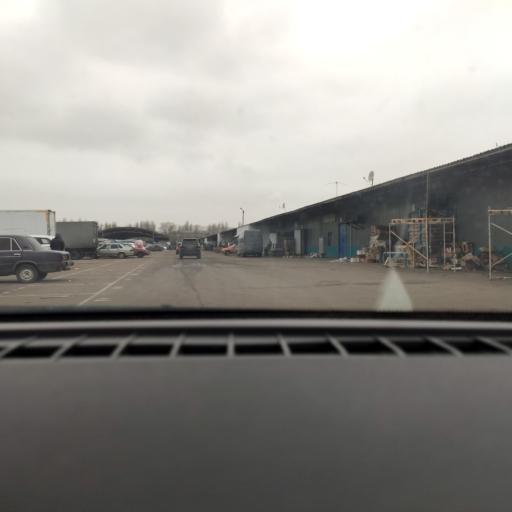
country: RU
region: Voronezj
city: Maslovka
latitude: 51.6122
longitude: 39.2627
